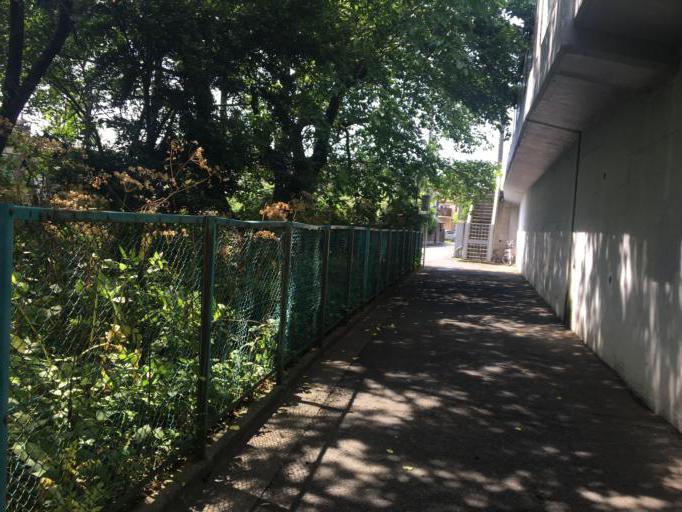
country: JP
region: Saitama
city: Tokorozawa
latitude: 35.7806
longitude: 139.4902
